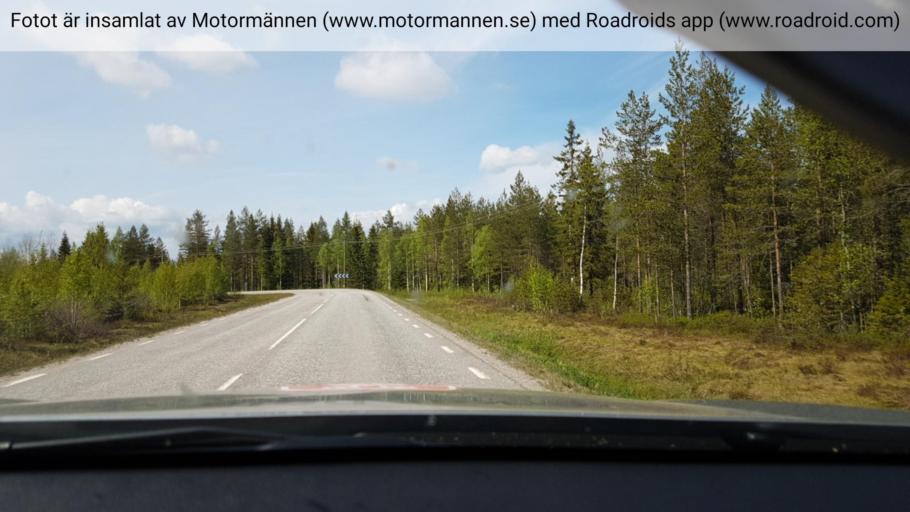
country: SE
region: Vaesterbotten
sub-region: Vannas Kommun
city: Vannasby
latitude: 63.8519
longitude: 19.9563
